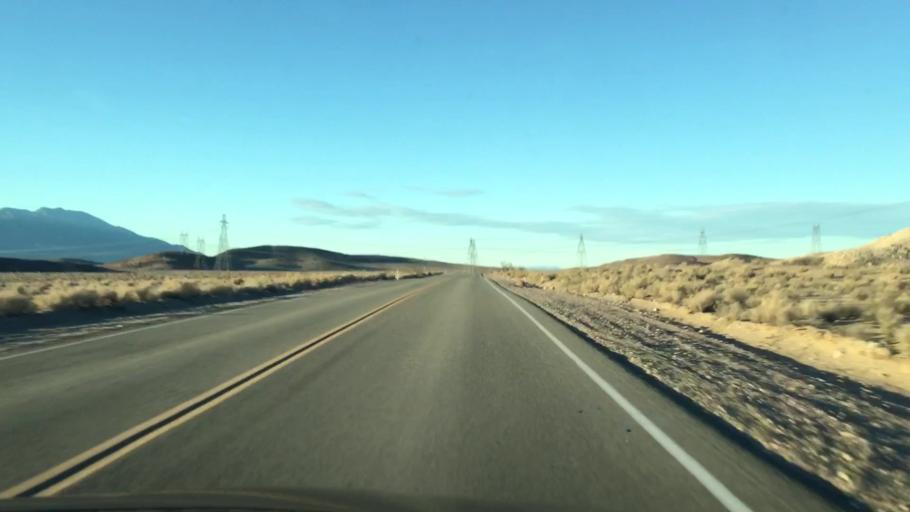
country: US
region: California
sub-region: San Bernardino County
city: Fort Irwin
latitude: 35.3799
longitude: -116.1231
